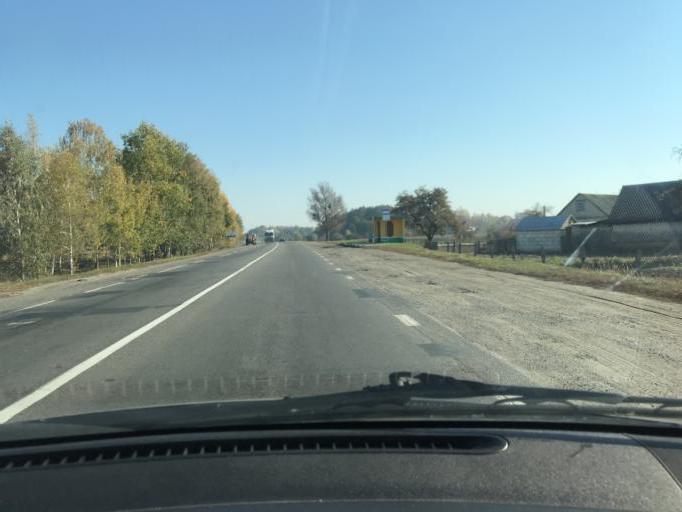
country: BY
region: Brest
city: Luninyets
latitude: 52.2746
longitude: 26.9272
